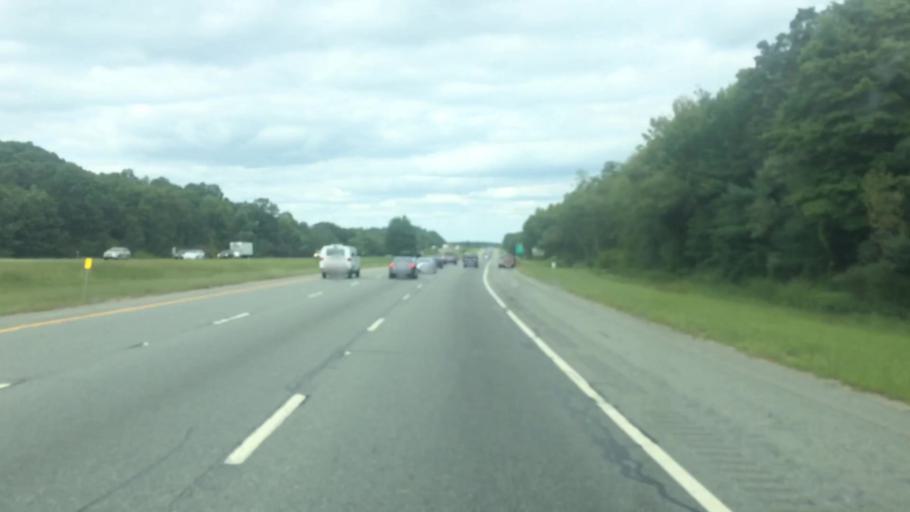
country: US
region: Rhode Island
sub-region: Providence County
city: Smithfield
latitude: 41.9321
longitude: -71.4996
